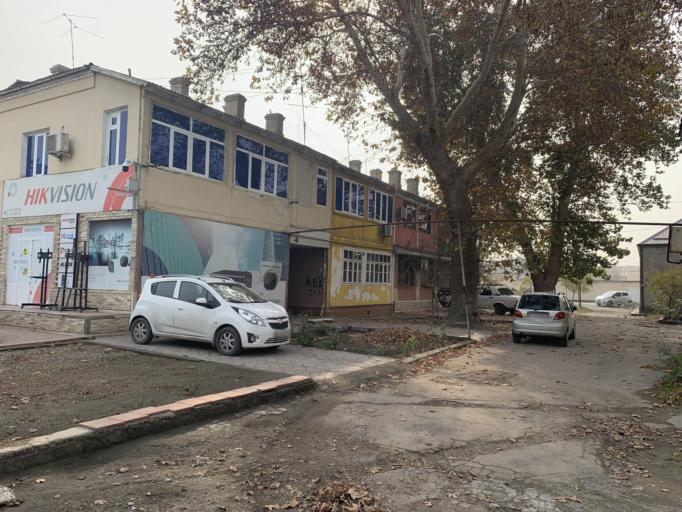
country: UZ
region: Fergana
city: Qo`qon
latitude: 40.5451
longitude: 70.9310
